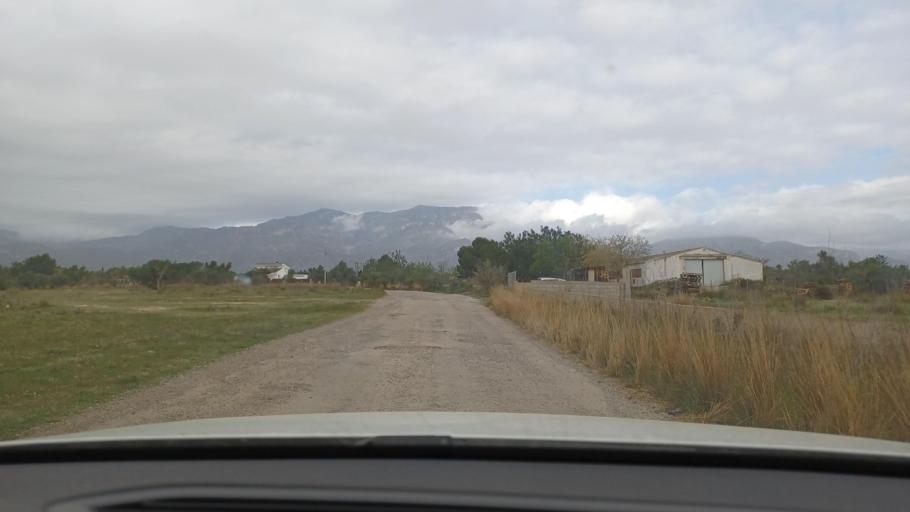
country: ES
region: Catalonia
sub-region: Provincia de Tarragona
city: Tortosa
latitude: 40.7920
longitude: 0.4669
